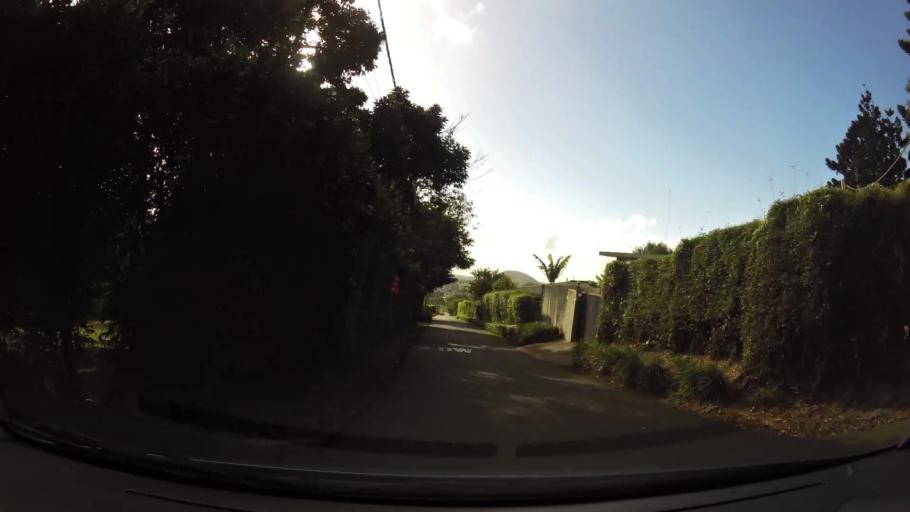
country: MU
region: Plaines Wilhems
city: Curepipe
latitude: -20.3155
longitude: 57.4990
